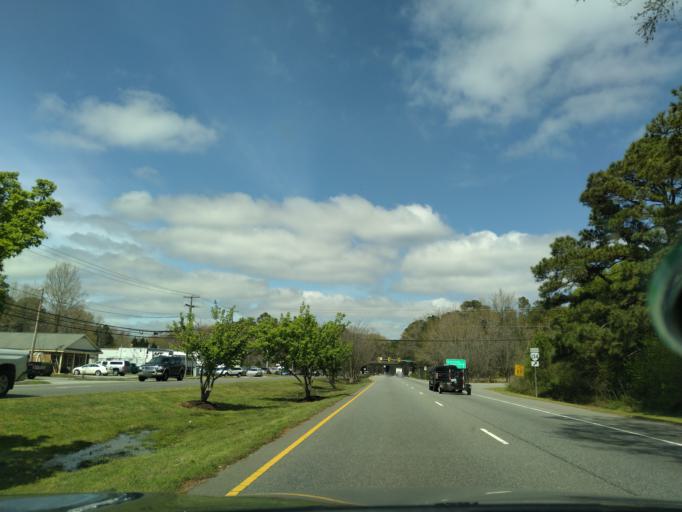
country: US
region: Virginia
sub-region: City of Poquoson
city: Poquoson
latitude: 37.1246
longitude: -76.4581
